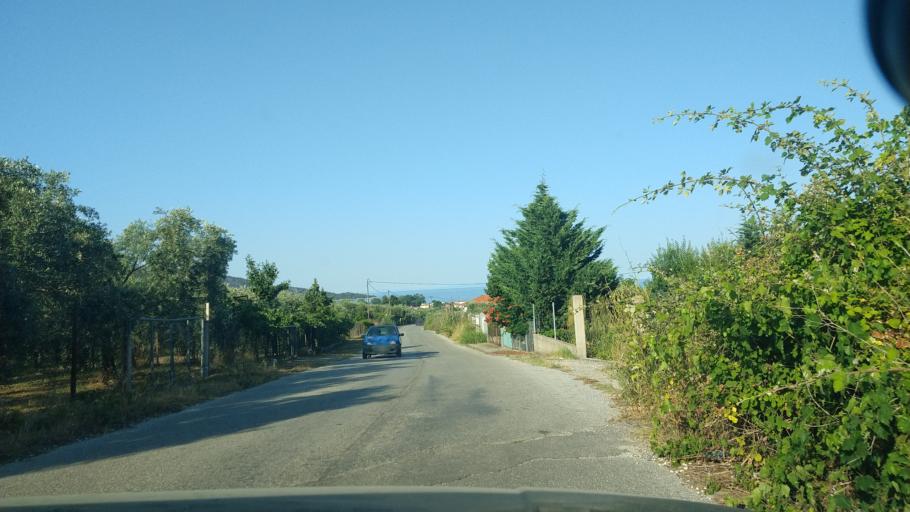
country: GR
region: East Macedonia and Thrace
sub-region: Nomos Kavalas
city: Potamia
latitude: 40.7159
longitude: 24.7413
